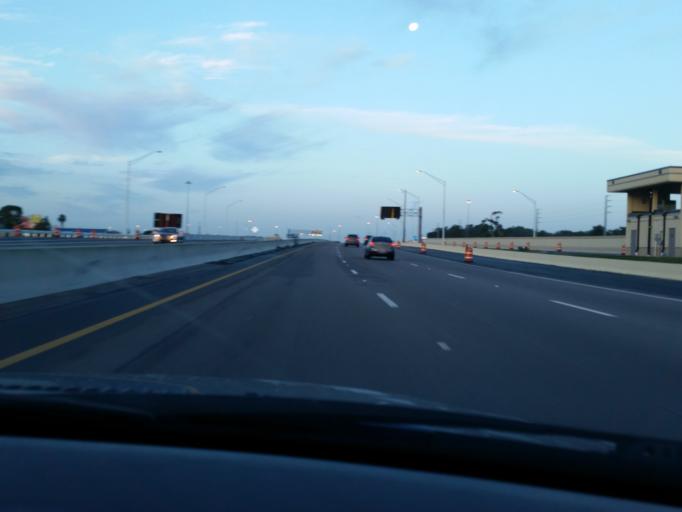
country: US
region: Florida
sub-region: Orange County
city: Belle Isle
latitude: 28.4506
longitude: -81.3424
